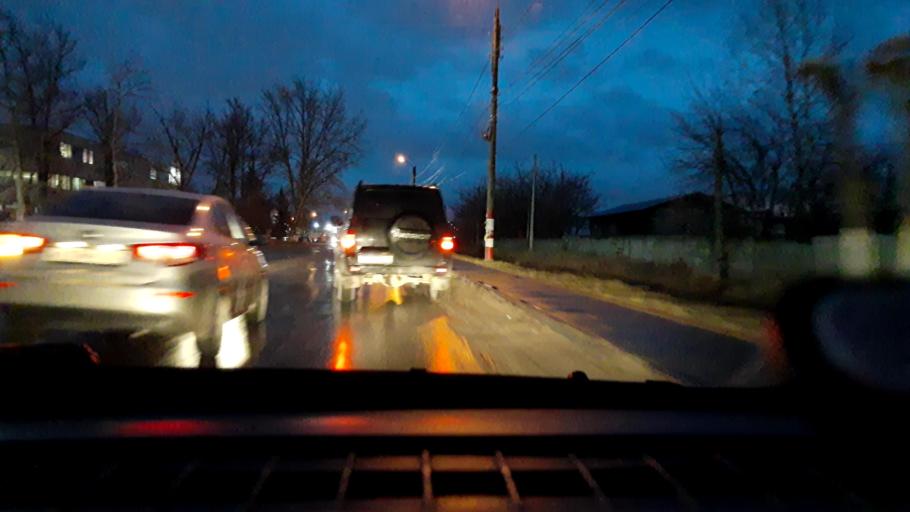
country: RU
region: Nizjnij Novgorod
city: Bor
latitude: 56.3500
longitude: 44.0789
